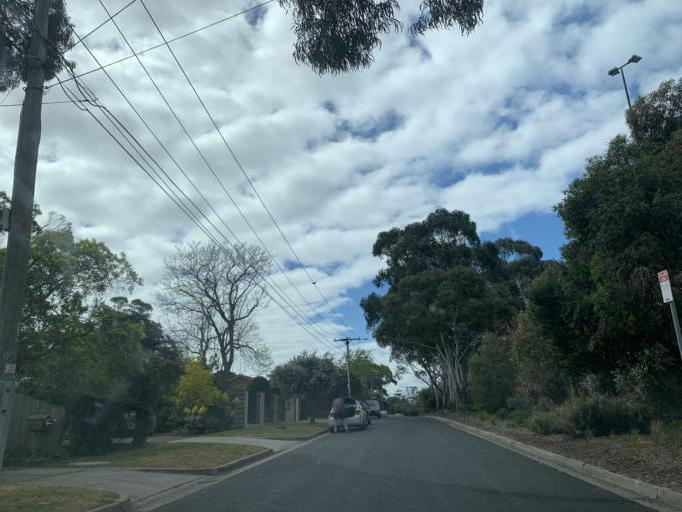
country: AU
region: Victoria
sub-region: Bayside
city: Cheltenham
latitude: -37.9696
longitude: 145.0475
